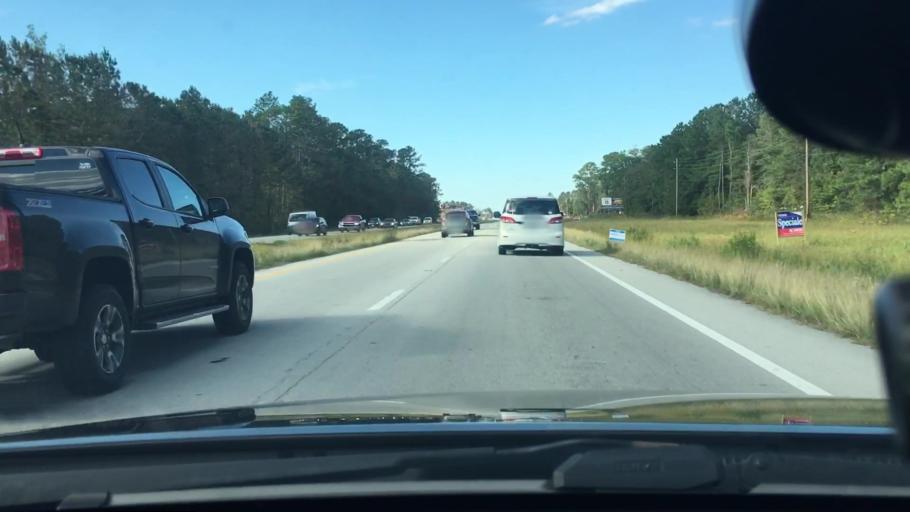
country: US
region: North Carolina
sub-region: Craven County
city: James City
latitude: 35.0521
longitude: -77.0152
